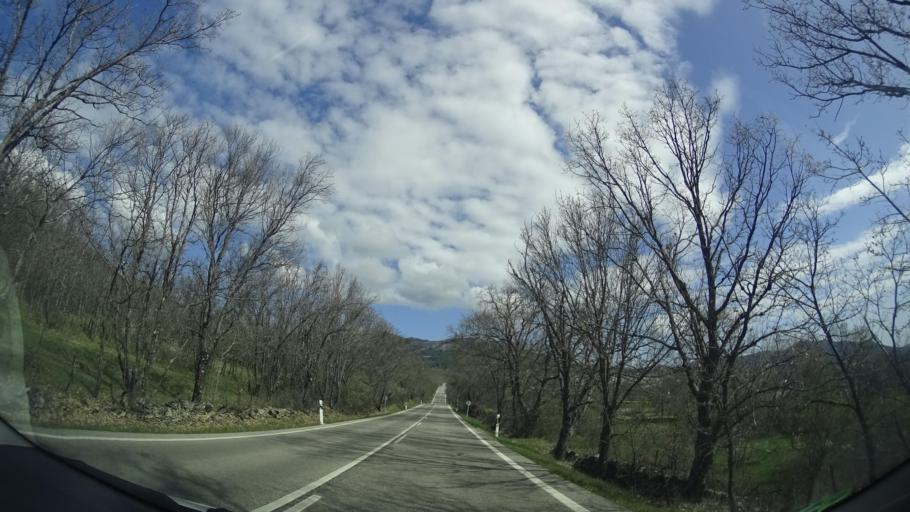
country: ES
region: Madrid
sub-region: Provincia de Madrid
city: Miraflores de la Sierra
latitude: 40.7950
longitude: -3.7748
